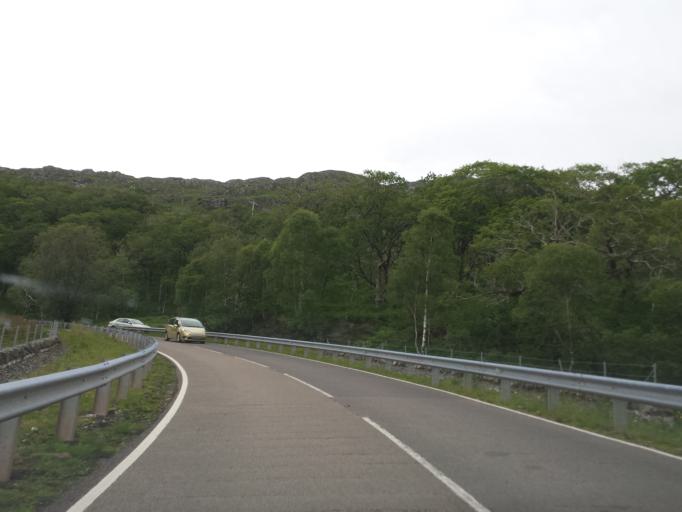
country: GB
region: Scotland
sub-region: Argyll and Bute
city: Isle Of Mull
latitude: 56.9011
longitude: -5.7527
